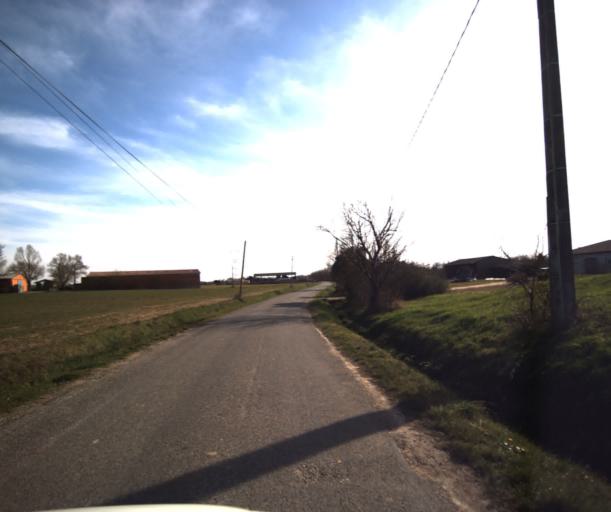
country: FR
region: Midi-Pyrenees
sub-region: Departement du Tarn-et-Garonne
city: Campsas
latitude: 43.9184
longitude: 1.3275
